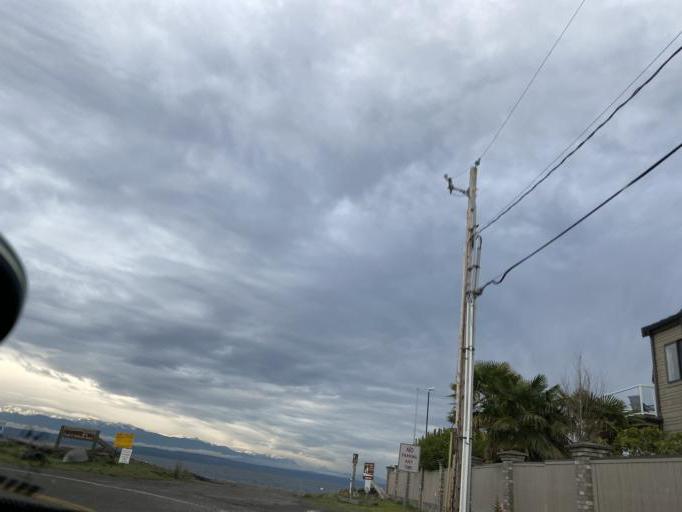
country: US
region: Washington
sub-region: Island County
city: Freeland
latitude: 47.9933
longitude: -122.5406
